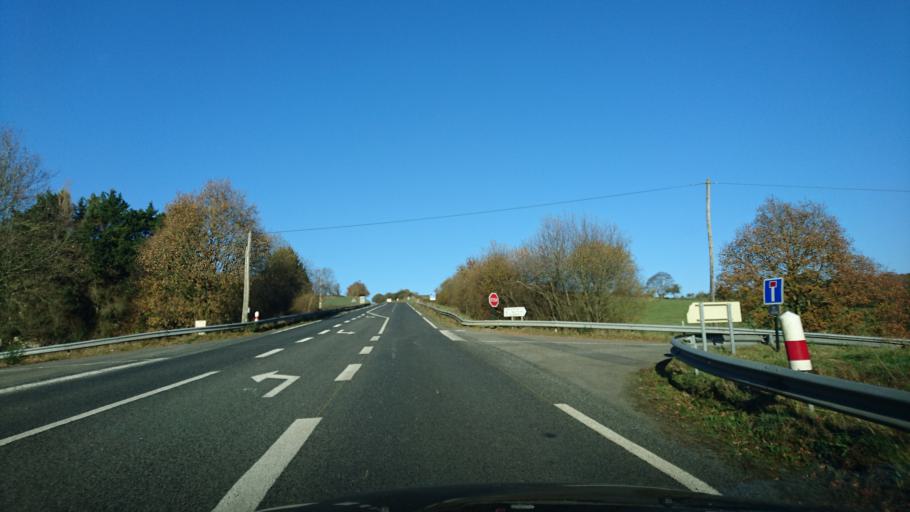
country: FR
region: Brittany
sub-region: Departement des Cotes-d'Armor
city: Pledran
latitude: 48.4681
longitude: -2.7518
